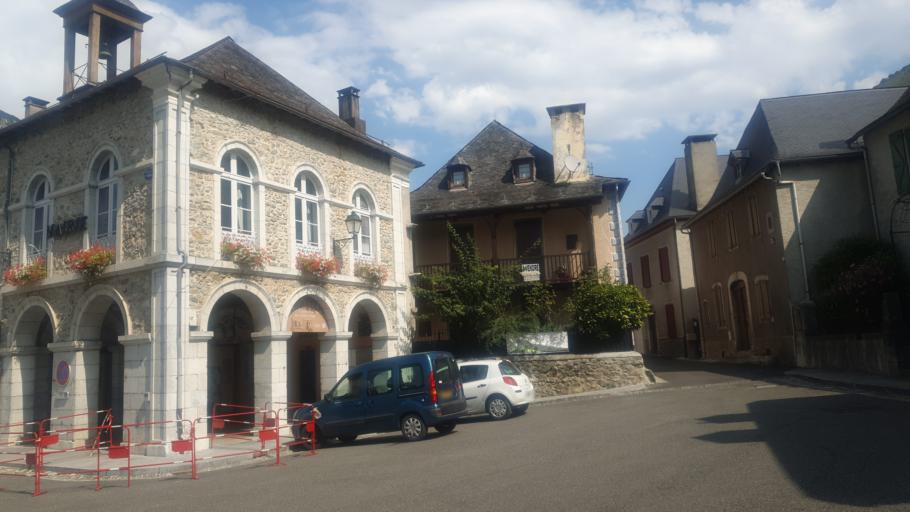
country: FR
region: Aquitaine
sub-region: Departement des Pyrenees-Atlantiques
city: Arette
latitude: 42.9987
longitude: -0.6001
